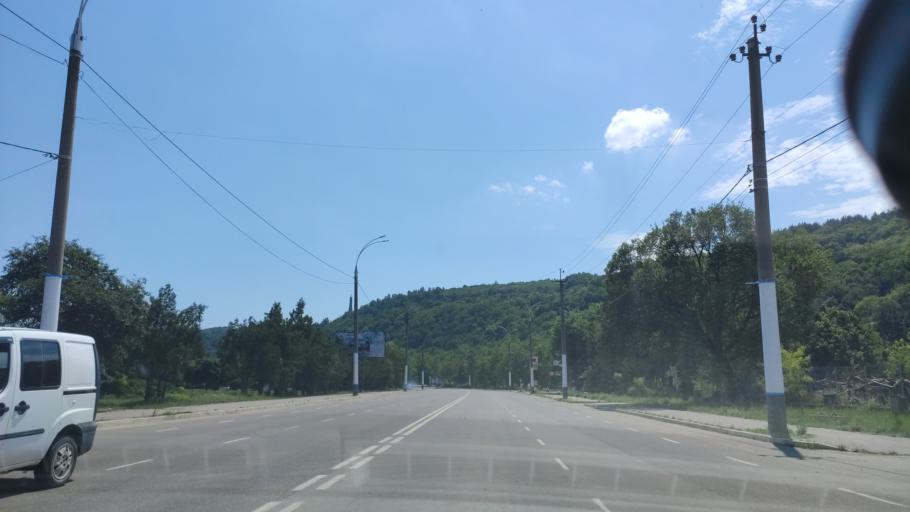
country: MD
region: Raionul Soroca
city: Soroca
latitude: 48.1456
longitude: 28.3021
